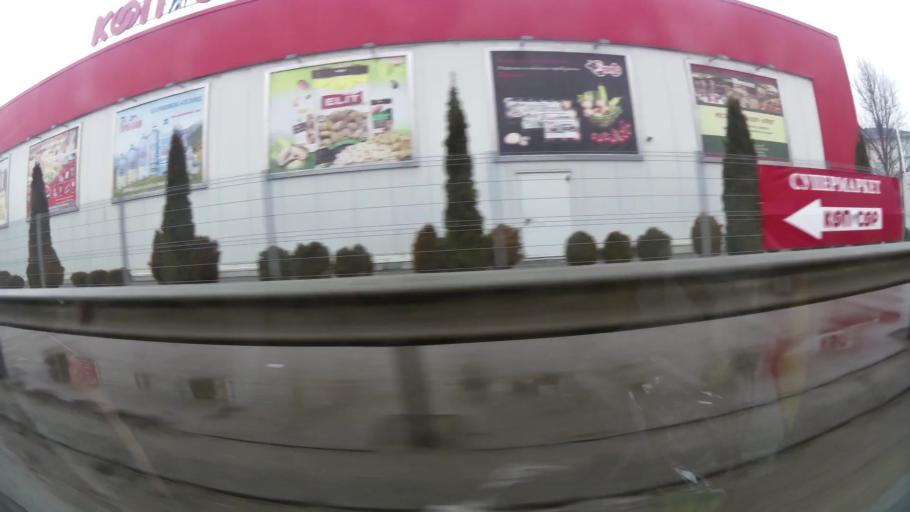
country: BG
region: Sofia-Capital
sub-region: Stolichna Obshtina
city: Sofia
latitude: 42.6871
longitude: 23.2730
